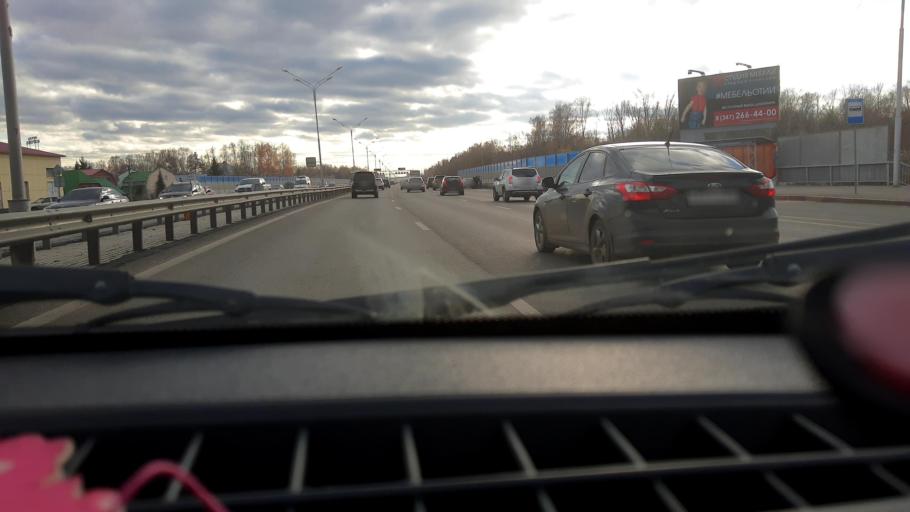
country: RU
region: Bashkortostan
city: Ufa
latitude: 54.6956
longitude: 55.9411
